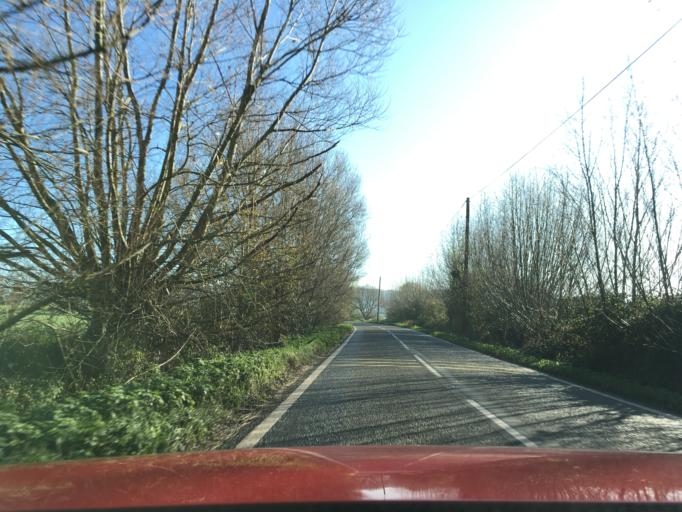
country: GB
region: England
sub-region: Somerset
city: Curry Rivel
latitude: 51.0812
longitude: -2.8764
